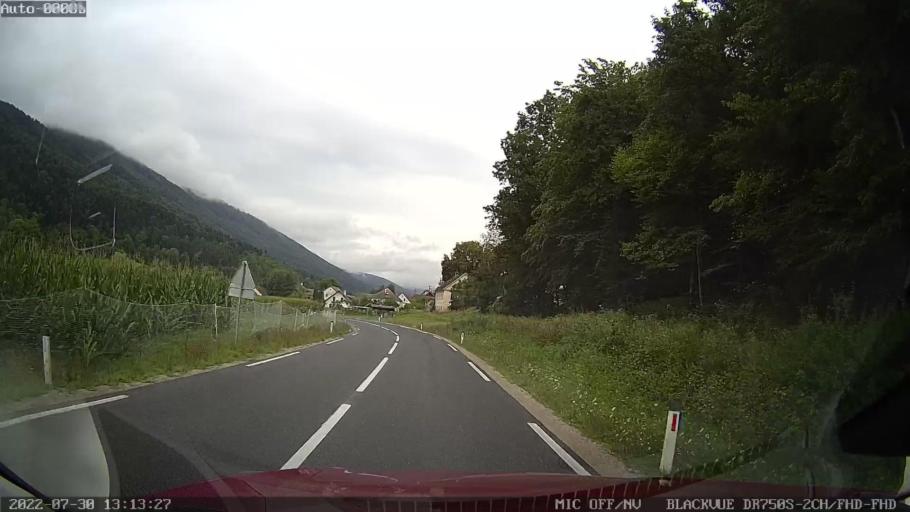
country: SI
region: Dolenjske Toplice
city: Dolenjske Toplice
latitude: 45.7212
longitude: 15.0579
